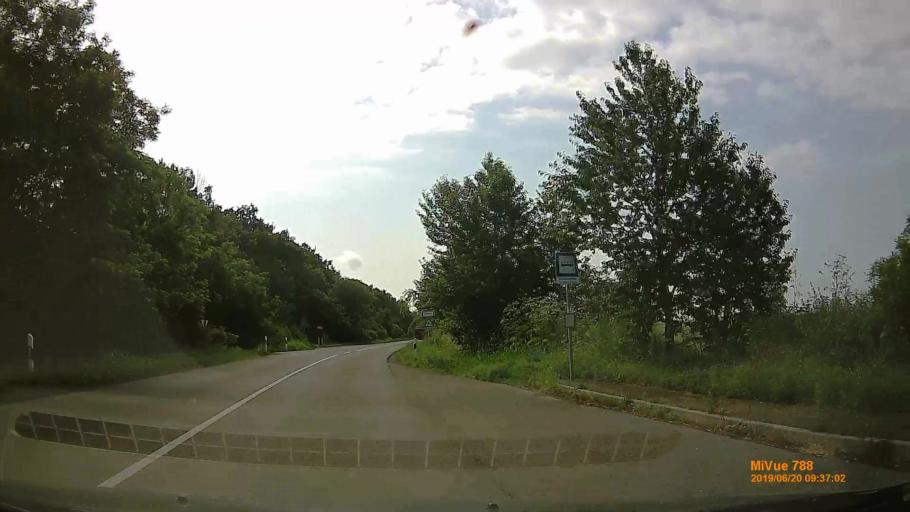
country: HU
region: Baranya
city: Pecsvarad
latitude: 46.1670
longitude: 18.4597
